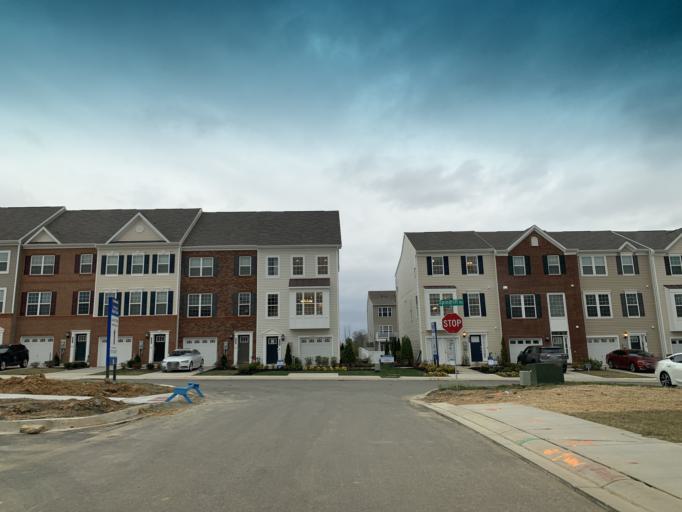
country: US
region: Maryland
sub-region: Harford County
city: Perryman
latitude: 39.4939
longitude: -76.2040
